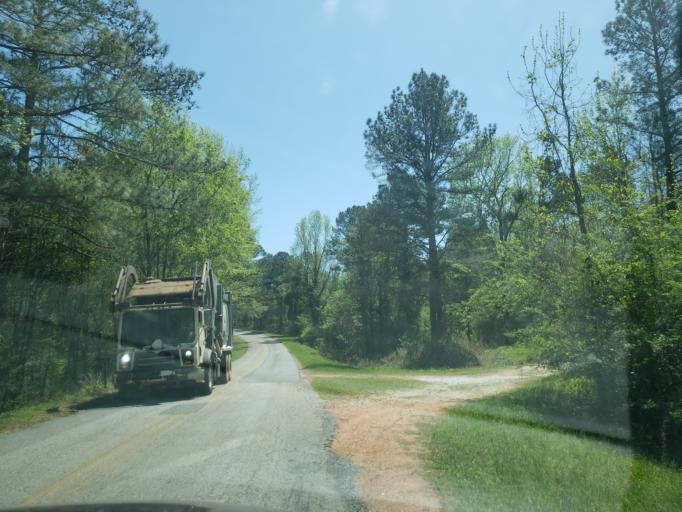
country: US
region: Alabama
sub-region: Tallapoosa County
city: Camp Hill
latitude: 32.6685
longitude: -85.7303
